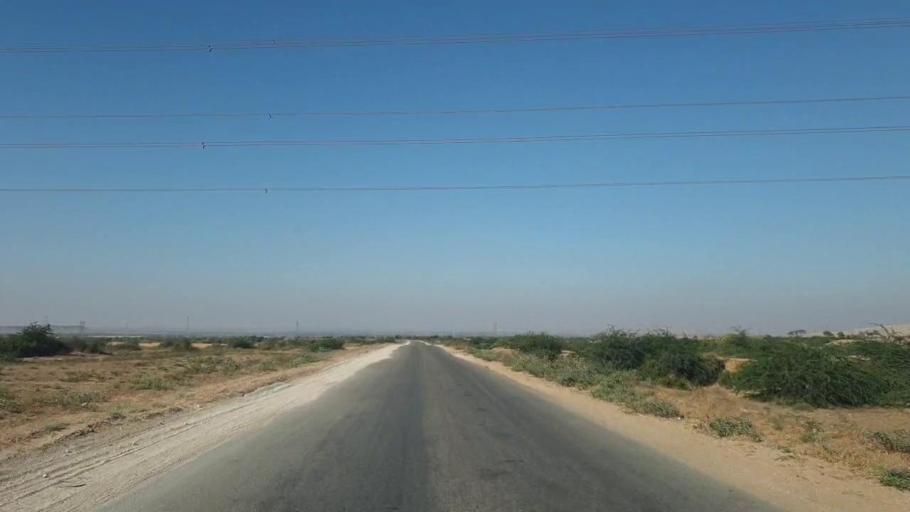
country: PK
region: Sindh
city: Gharo
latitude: 25.1629
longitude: 67.6628
